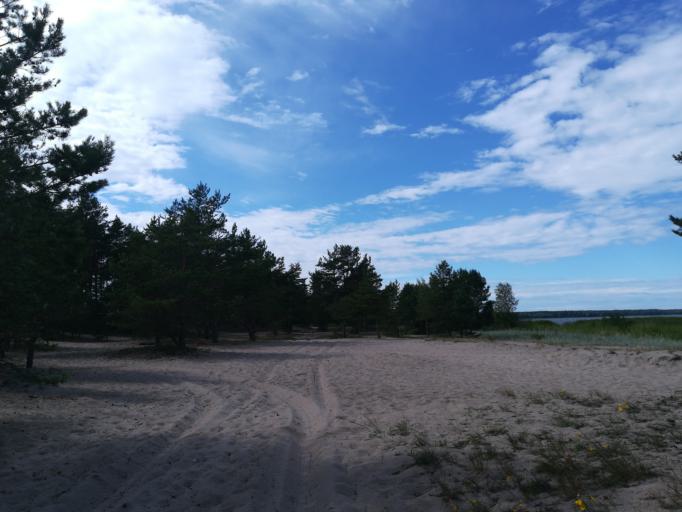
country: RU
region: Leningrad
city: Ust'-Luga
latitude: 59.6811
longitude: 28.2317
